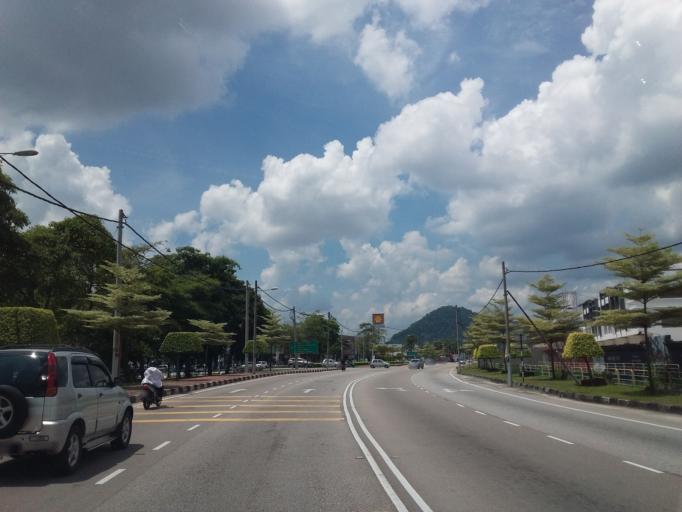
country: MY
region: Johor
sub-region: Daerah Batu Pahat
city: Batu Pahat
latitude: 1.8596
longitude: 102.9278
